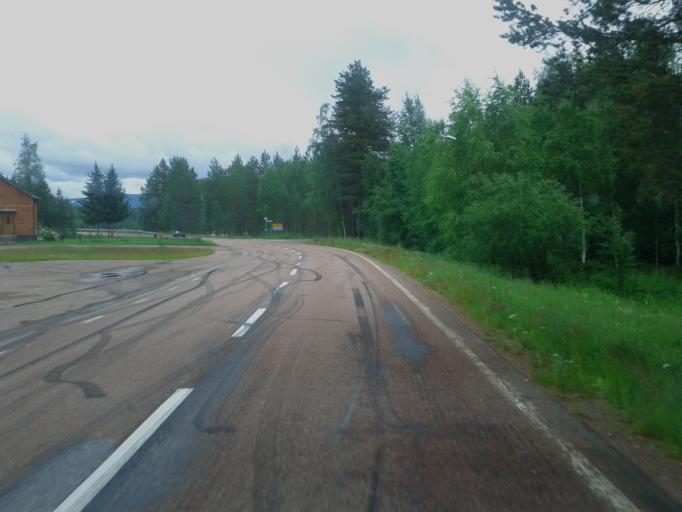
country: NO
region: Hedmark
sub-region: Trysil
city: Innbygda
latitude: 61.8516
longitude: 12.7092
